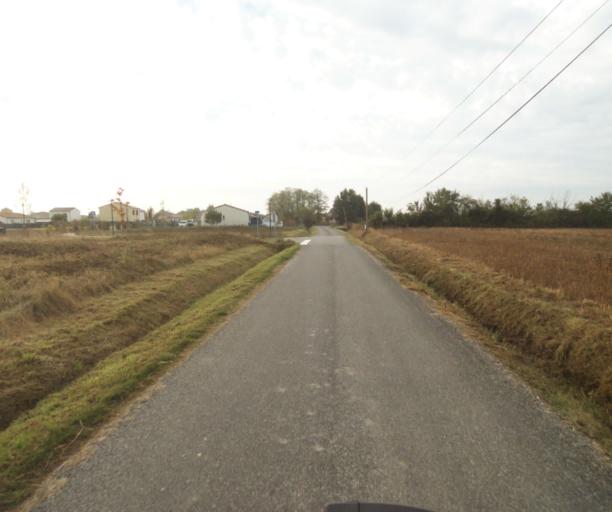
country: FR
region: Midi-Pyrenees
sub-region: Departement du Tarn-et-Garonne
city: Montech
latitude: 43.9472
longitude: 1.2314
